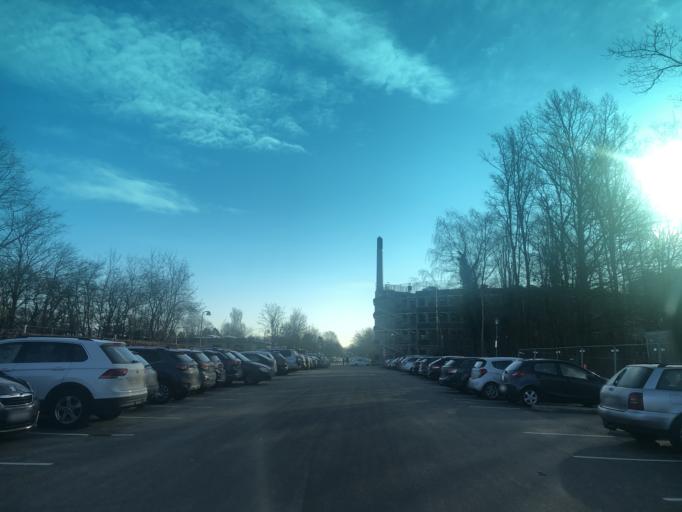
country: DK
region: Capital Region
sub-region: Glostrup Kommune
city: Glostrup
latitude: 55.6722
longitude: 12.3844
